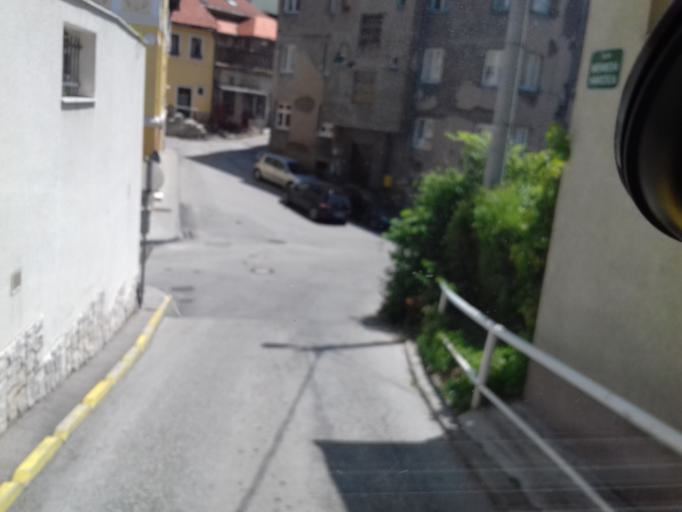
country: BA
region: Federation of Bosnia and Herzegovina
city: Kobilja Glava
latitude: 43.8634
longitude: 18.4252
